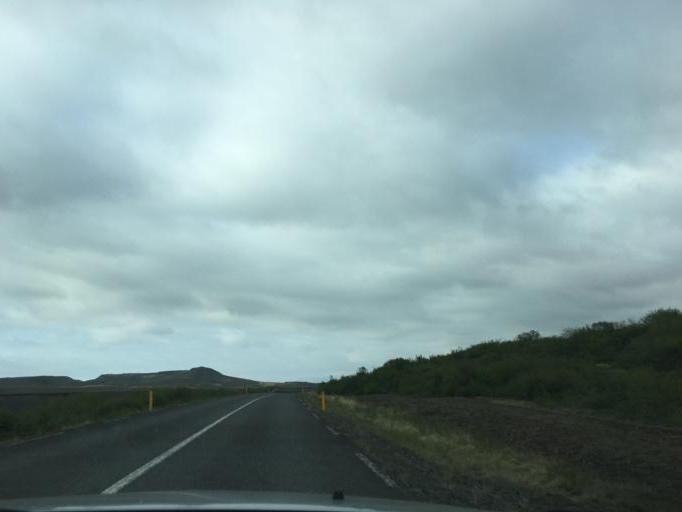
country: IS
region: South
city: Vestmannaeyjar
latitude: 64.2620
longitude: -20.2198
